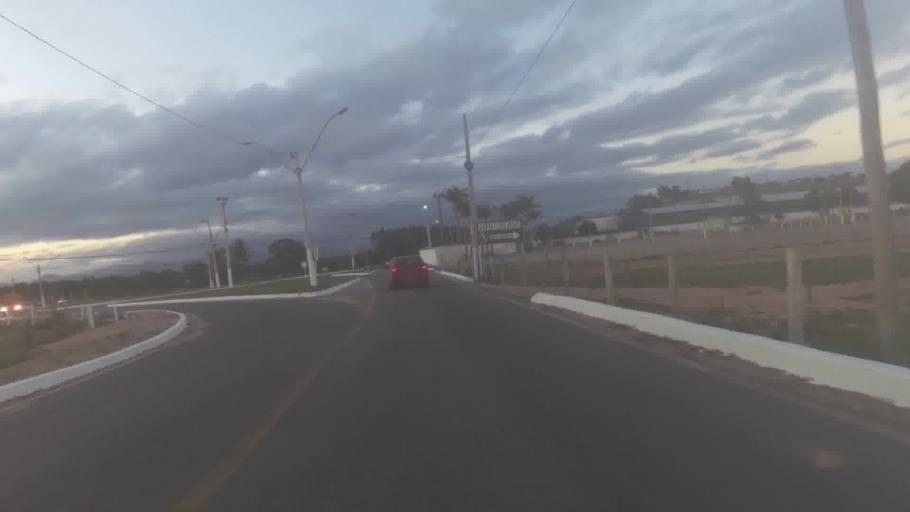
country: BR
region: Espirito Santo
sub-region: Itapemirim
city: Itapemirim
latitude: -21.0214
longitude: -40.8383
